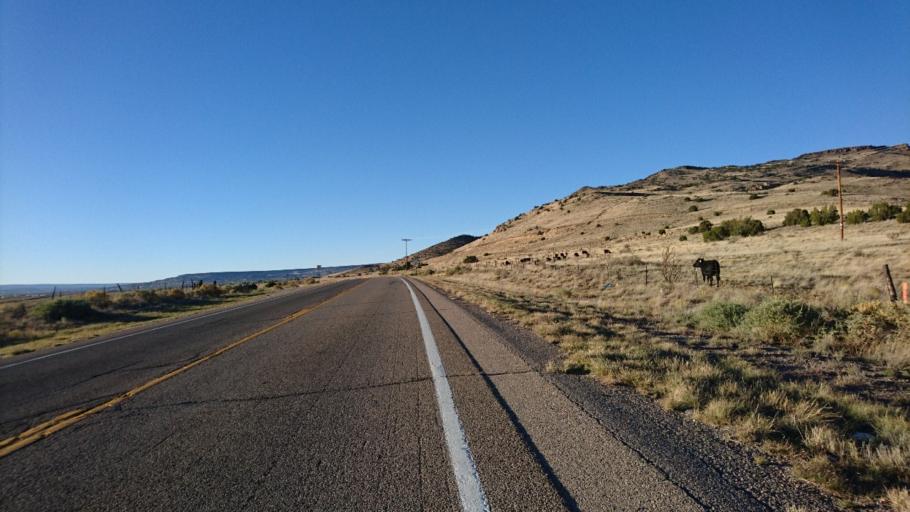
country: US
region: New Mexico
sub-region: Cibola County
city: Grants
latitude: 35.1122
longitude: -107.7828
